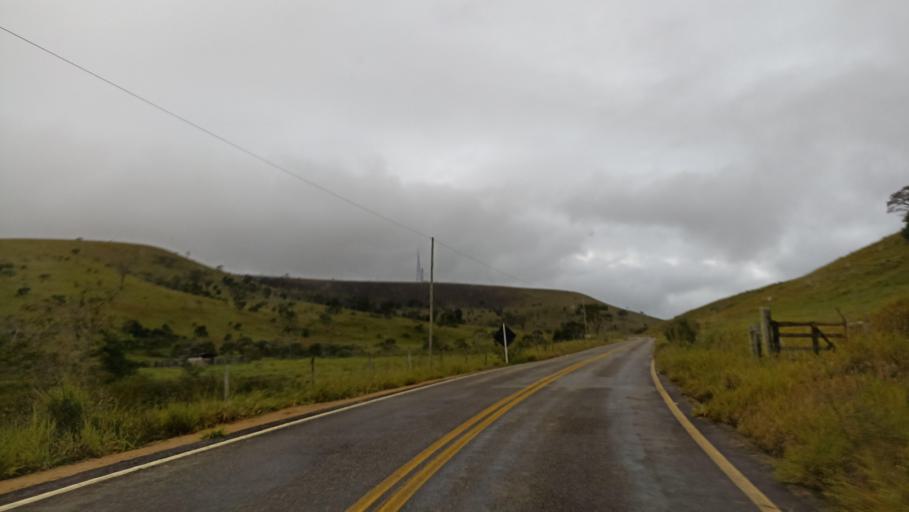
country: BR
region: Minas Gerais
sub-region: Joaima
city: Joaima
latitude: -16.6744
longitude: -40.5259
